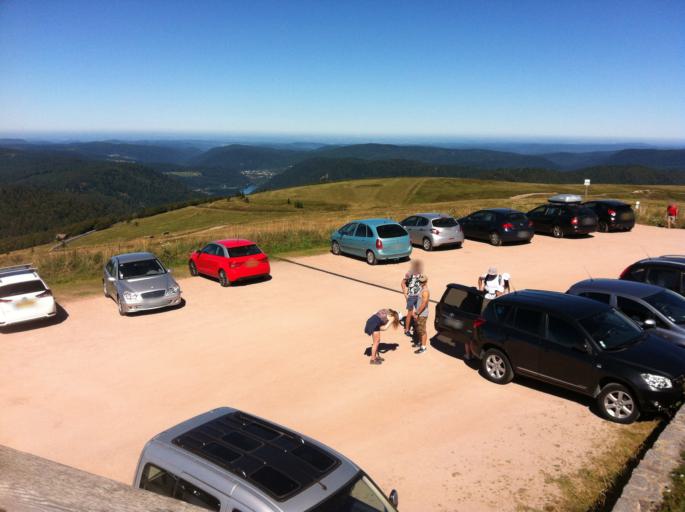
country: FR
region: Alsace
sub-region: Departement du Haut-Rhin
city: Metzeral
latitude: 48.0376
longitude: 7.0153
